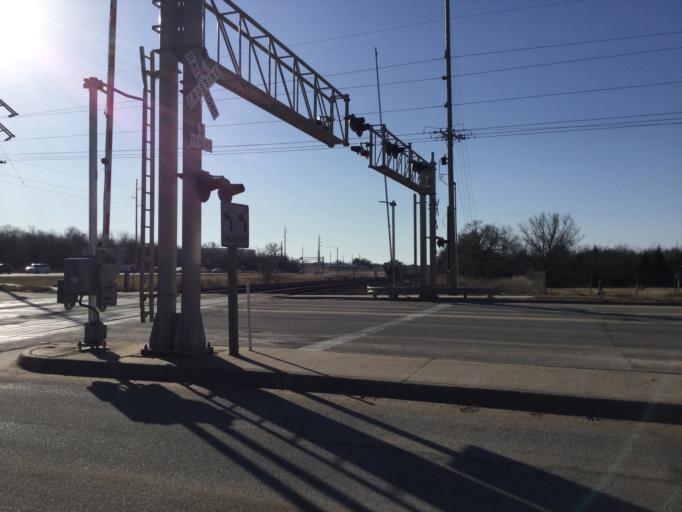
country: US
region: Kansas
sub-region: Sedgwick County
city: Derby
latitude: 37.6205
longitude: -97.2951
